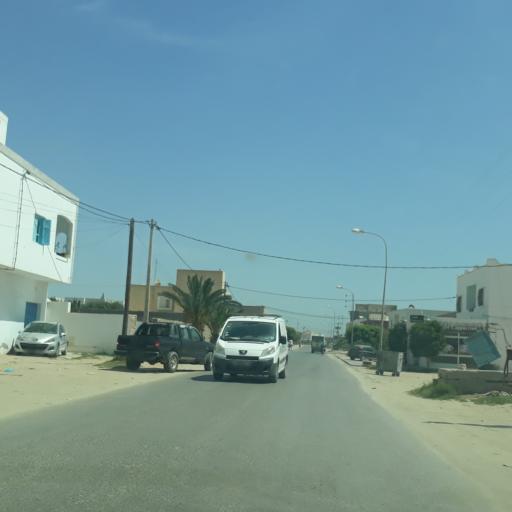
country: TN
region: Safaqis
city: Al Qarmadah
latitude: 34.8201
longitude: 10.7781
